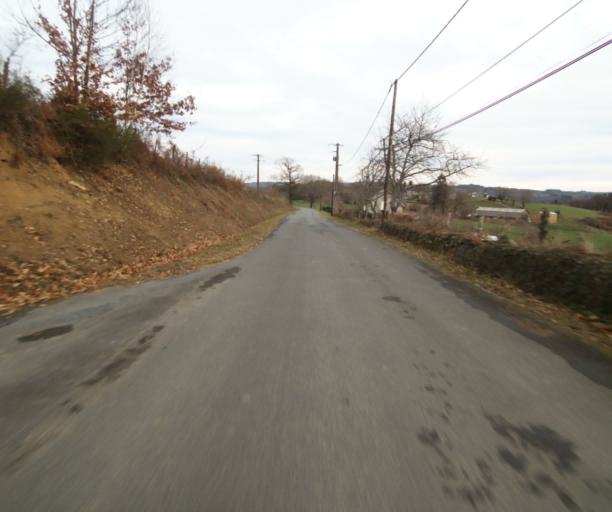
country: FR
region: Limousin
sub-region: Departement de la Correze
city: Chameyrat
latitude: 45.2353
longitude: 1.6901
